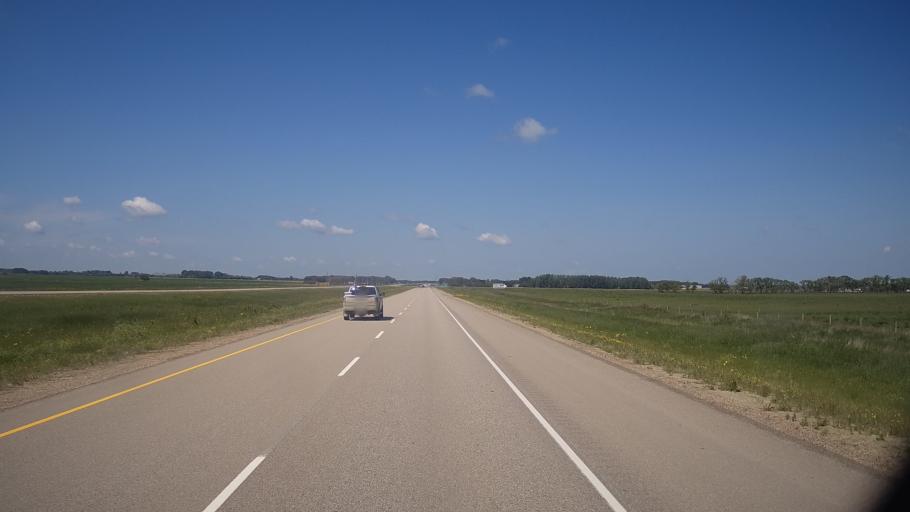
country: CA
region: Saskatchewan
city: Saskatoon
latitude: 52.0123
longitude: -106.3715
